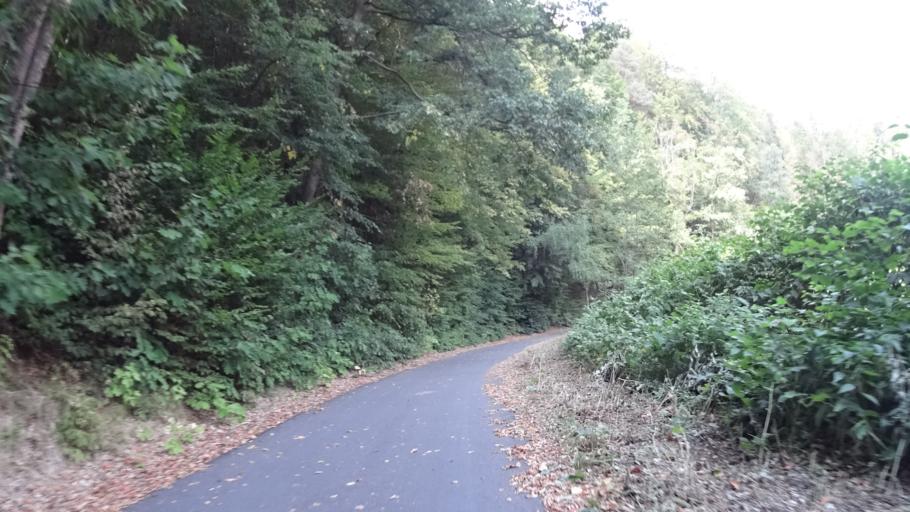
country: DE
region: Saxony
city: Schlegel
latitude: 50.9714
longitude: 14.9028
